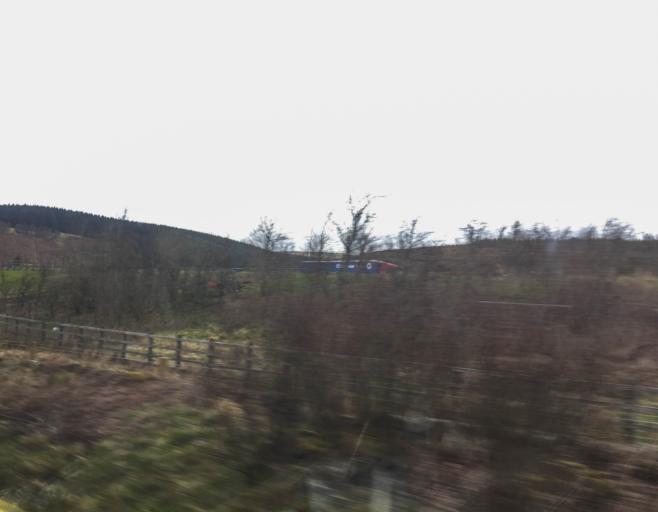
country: GB
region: Scotland
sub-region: Dumfries and Galloway
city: Moffat
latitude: 55.4254
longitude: -3.6003
